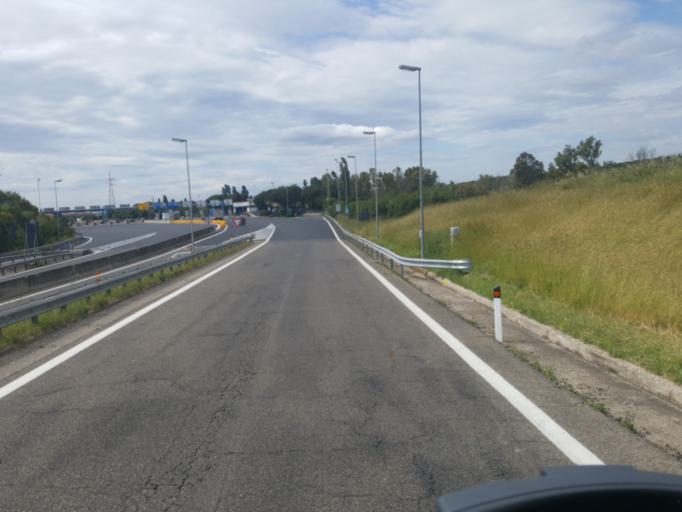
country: IT
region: Latium
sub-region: Citta metropolitana di Roma Capitale
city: Ara Nova
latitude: 41.9140
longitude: 12.2137
